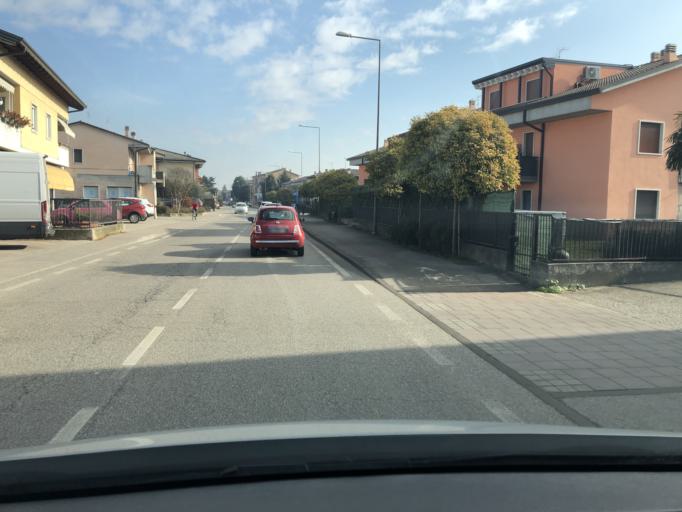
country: IT
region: Veneto
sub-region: Provincia di Verona
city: Lugagnano
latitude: 45.4321
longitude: 10.8817
